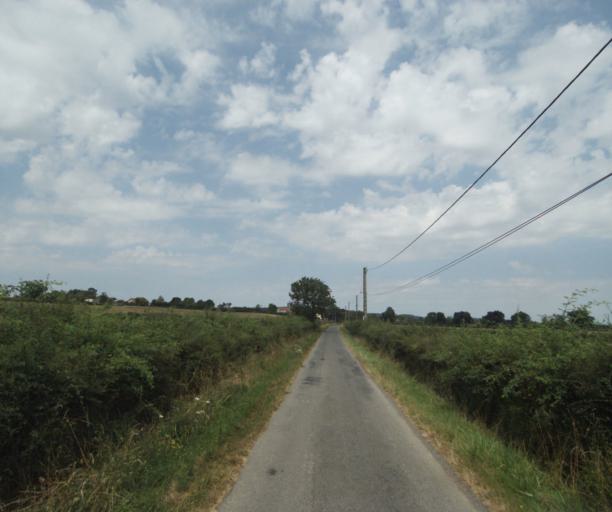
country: FR
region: Bourgogne
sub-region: Departement de Saone-et-Loire
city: Gueugnon
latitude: 46.5857
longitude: 4.0413
